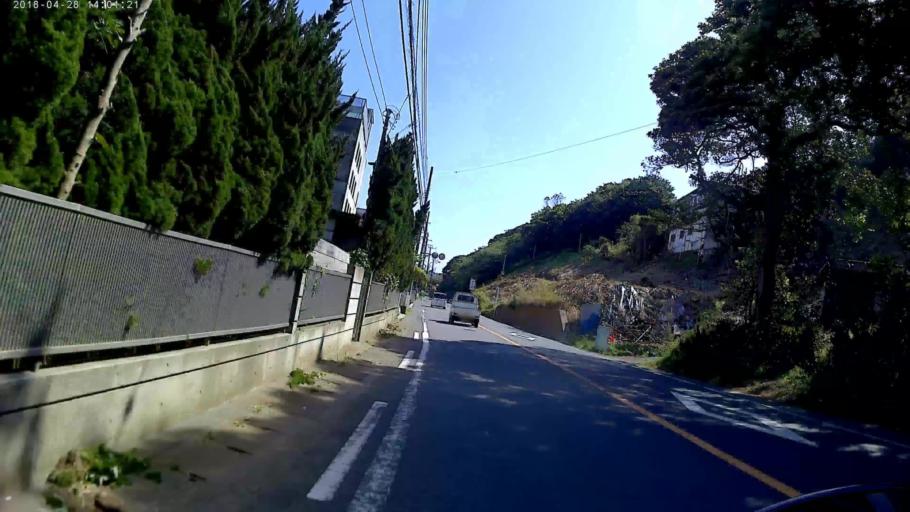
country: JP
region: Kanagawa
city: Miura
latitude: 35.1688
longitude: 139.6593
